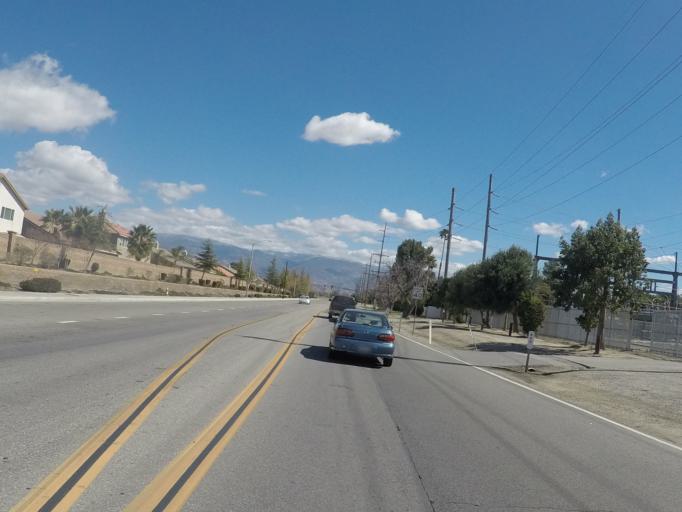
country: US
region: California
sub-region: Riverside County
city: Hemet
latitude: 33.7729
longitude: -116.9886
